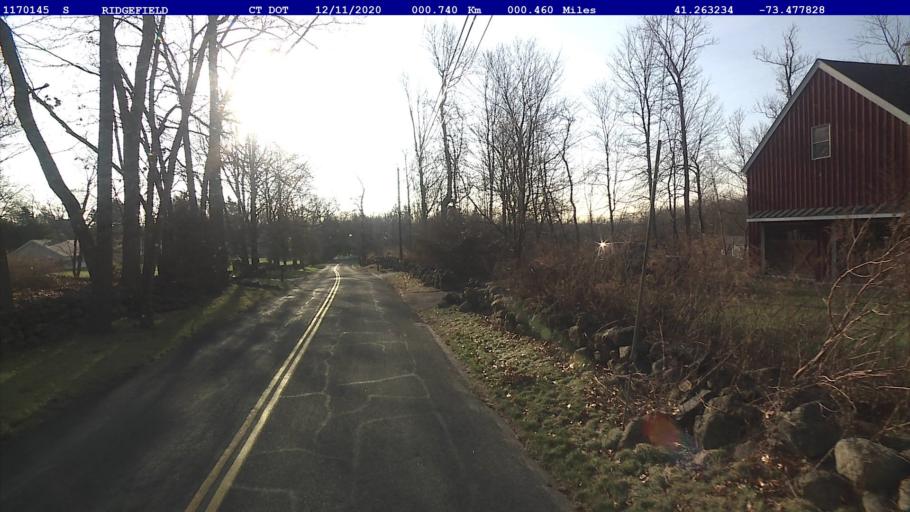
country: US
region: Connecticut
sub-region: Fairfield County
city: Ridgefield
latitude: 41.2632
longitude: -73.4778
